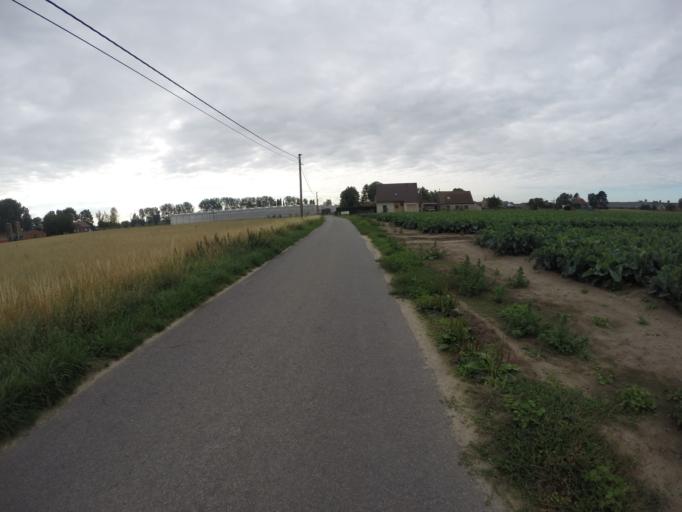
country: BE
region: Flanders
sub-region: Provincie West-Vlaanderen
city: Ruiselede
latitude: 51.0533
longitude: 3.4198
